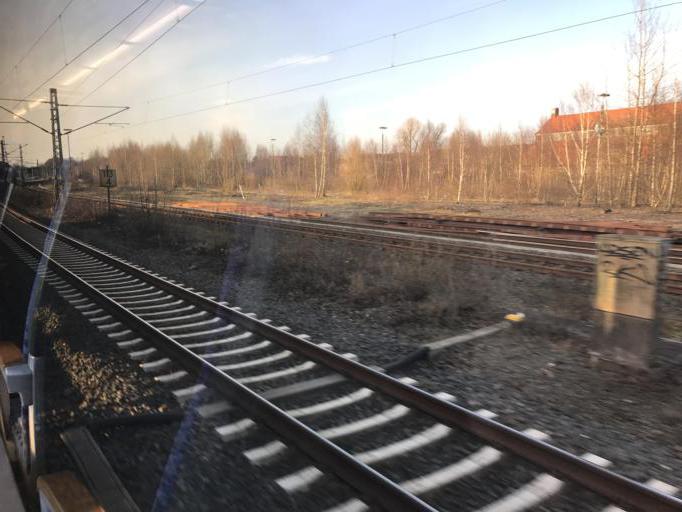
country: DE
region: Schleswig-Holstein
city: Rendsburg
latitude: 54.2992
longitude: 9.6750
